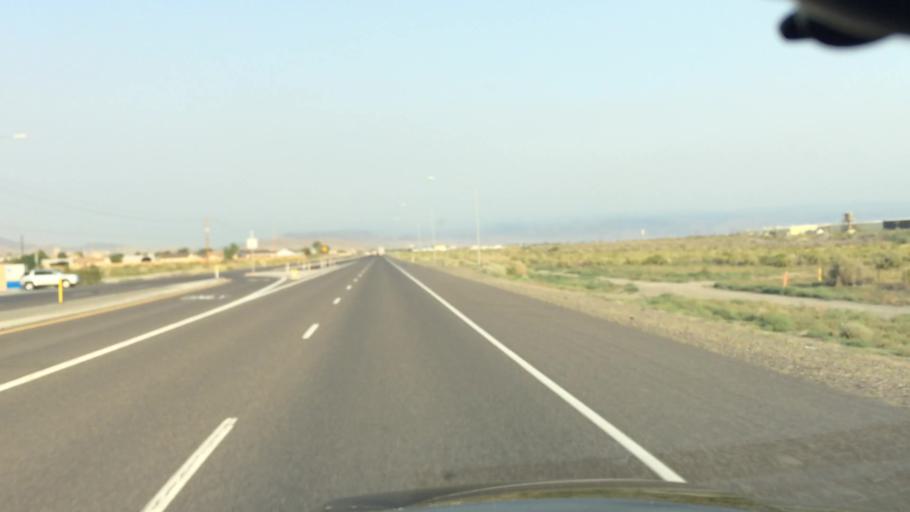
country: US
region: Nevada
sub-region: Lyon County
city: Fernley
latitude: 39.5983
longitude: -119.1966
